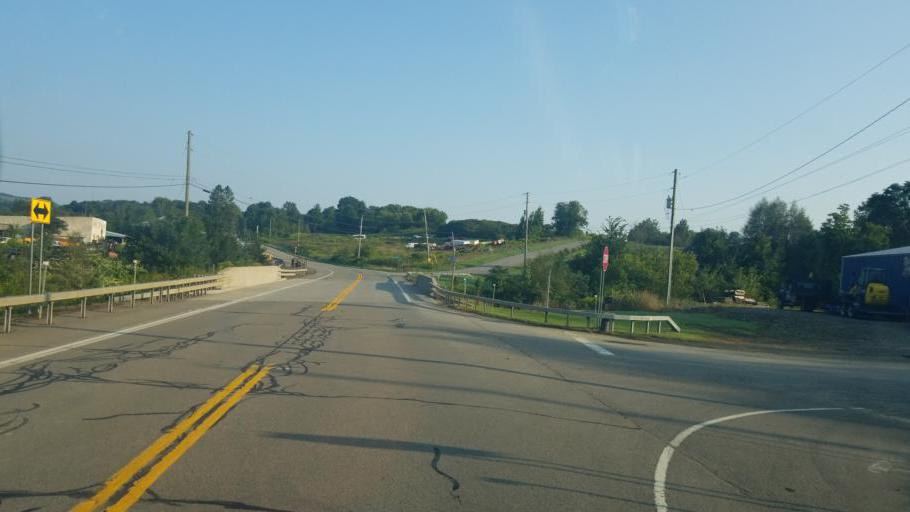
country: US
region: Pennsylvania
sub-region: Tioga County
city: Westfield
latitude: 42.0175
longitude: -77.5216
